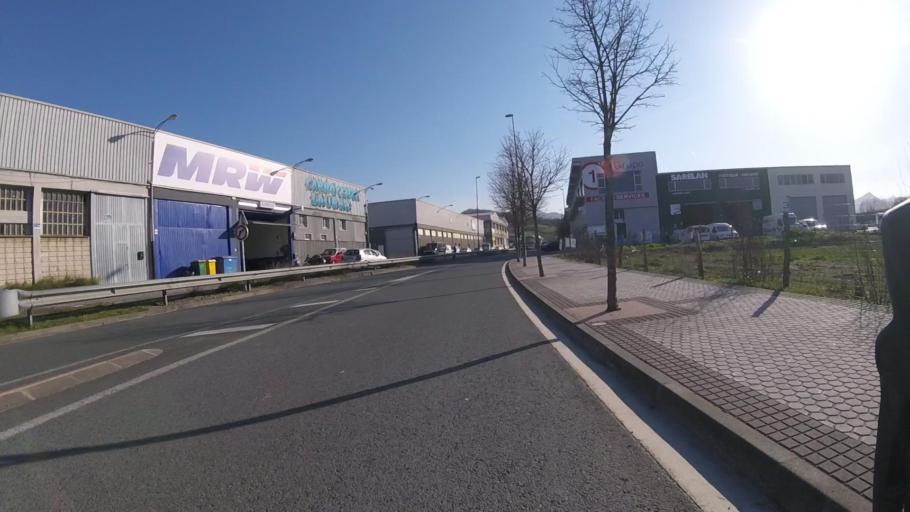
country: ES
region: Basque Country
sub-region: Provincia de Guipuzcoa
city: Astigarraga
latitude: 43.2752
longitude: -1.9543
